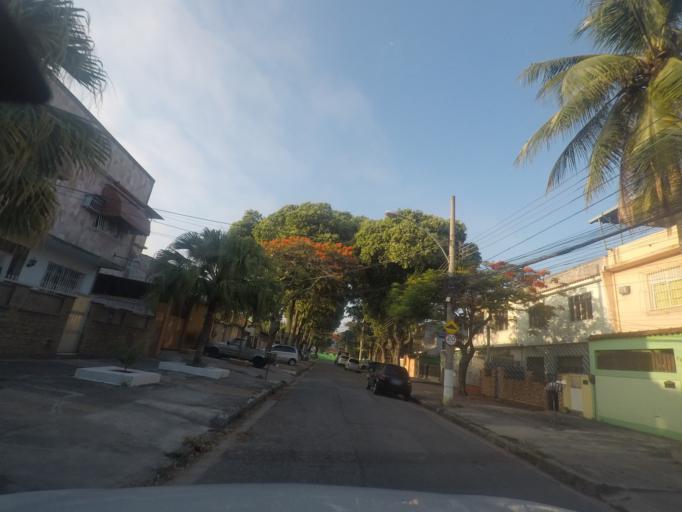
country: BR
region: Rio de Janeiro
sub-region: Duque De Caxias
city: Duque de Caxias
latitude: -22.8321
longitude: -43.2717
